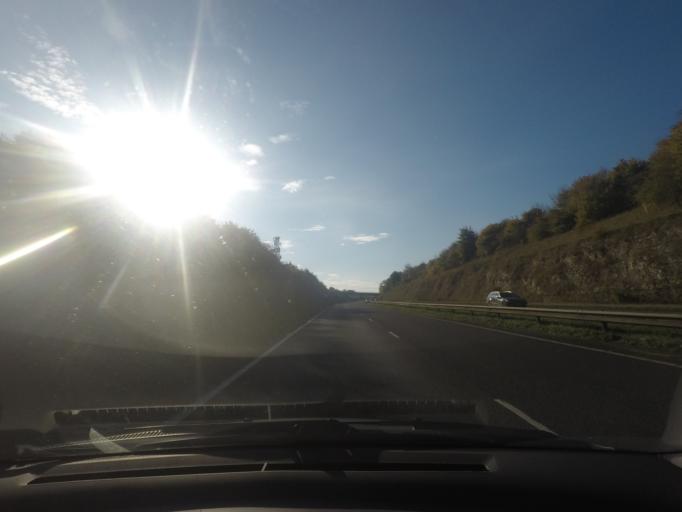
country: GB
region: England
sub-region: North Lincolnshire
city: Barton upon Humber
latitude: 53.6660
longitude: -0.4492
